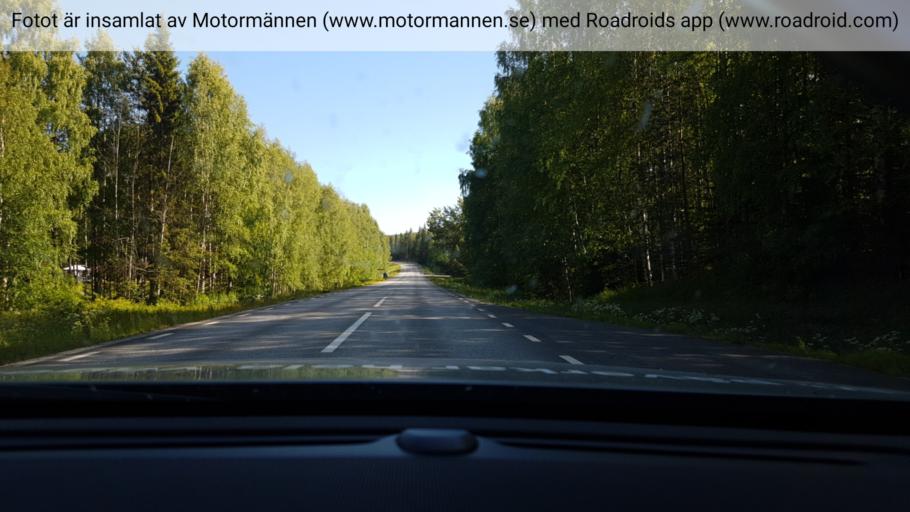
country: SE
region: Vaesterbotten
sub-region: Lycksele Kommun
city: Lycksele
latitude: 64.6618
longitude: 18.4480
